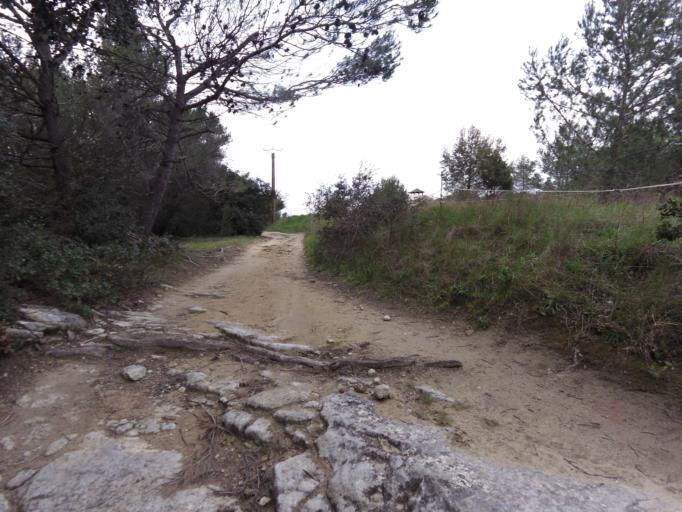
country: FR
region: Languedoc-Roussillon
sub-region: Departement du Gard
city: Aigues-Vives
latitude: 43.7356
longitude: 4.1660
